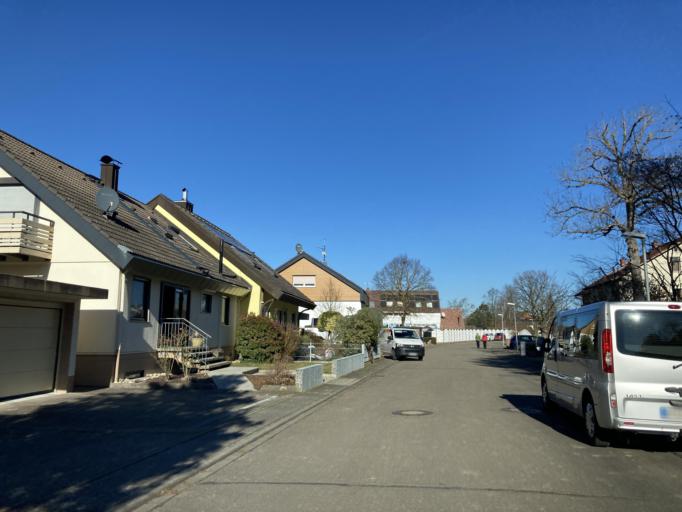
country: DE
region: Baden-Wuerttemberg
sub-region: Freiburg Region
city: Eichstetten
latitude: 48.1020
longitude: 7.7728
